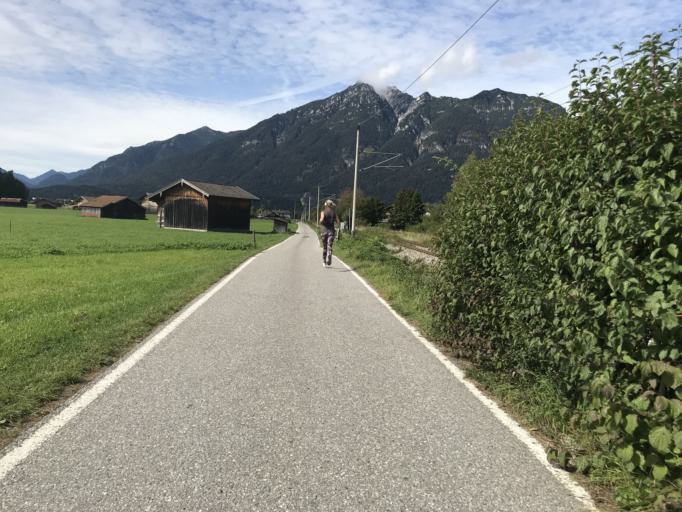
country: DE
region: Bavaria
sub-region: Upper Bavaria
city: Garmisch-Partenkirchen
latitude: 47.4839
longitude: 11.1099
